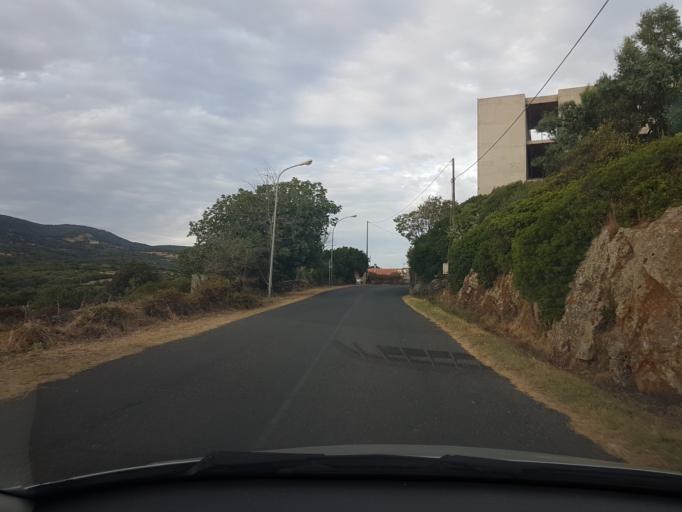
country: IT
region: Sardinia
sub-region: Provincia di Oristano
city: Seneghe
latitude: 40.0821
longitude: 8.6068
